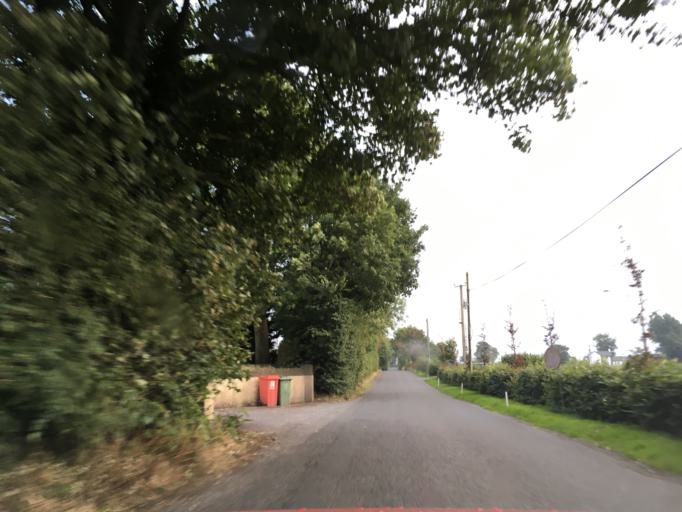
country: IE
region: Munster
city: Cashel
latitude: 52.4927
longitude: -7.9743
